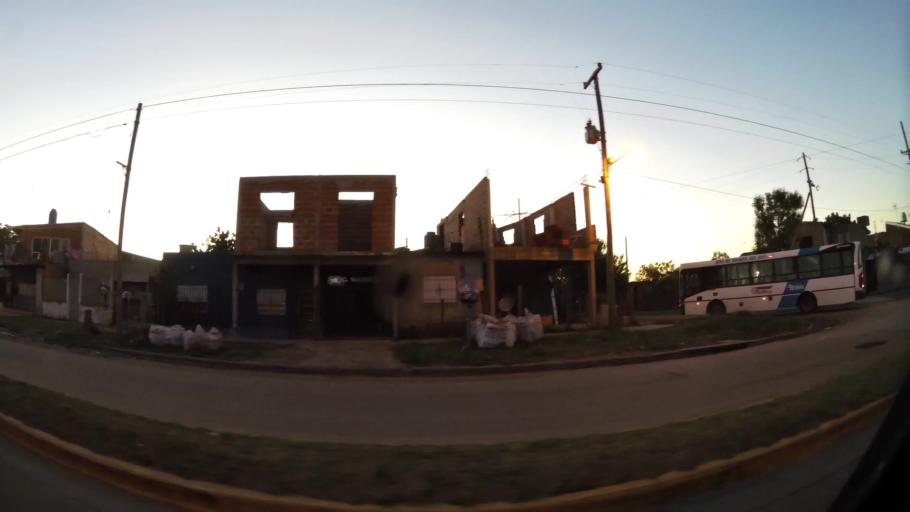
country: AR
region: Buenos Aires
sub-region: Partido de Almirante Brown
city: Adrogue
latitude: -34.7851
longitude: -58.3237
